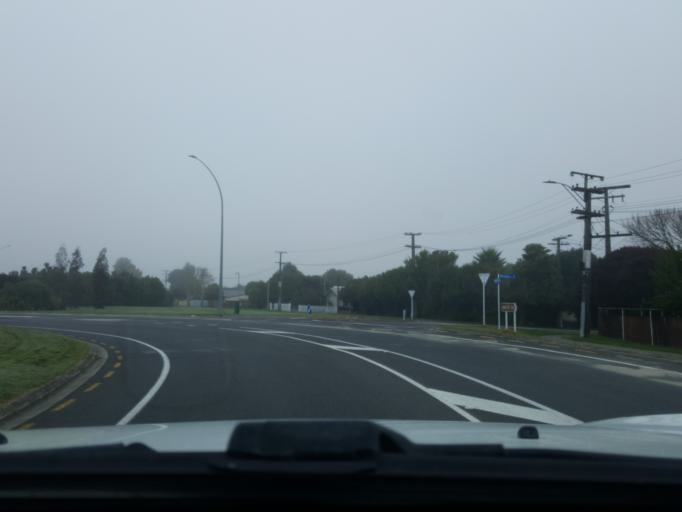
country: NZ
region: Waikato
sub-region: Hamilton City
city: Hamilton
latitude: -37.7702
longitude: 175.2394
